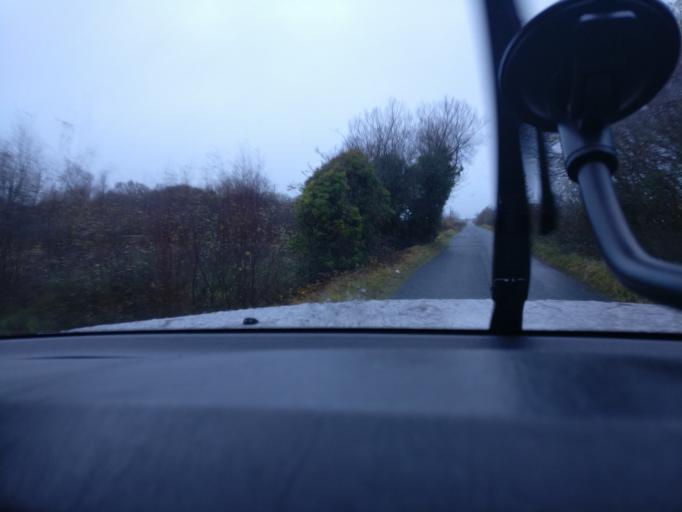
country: IE
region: Connaught
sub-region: County Galway
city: Loughrea
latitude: 53.2349
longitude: -8.5241
